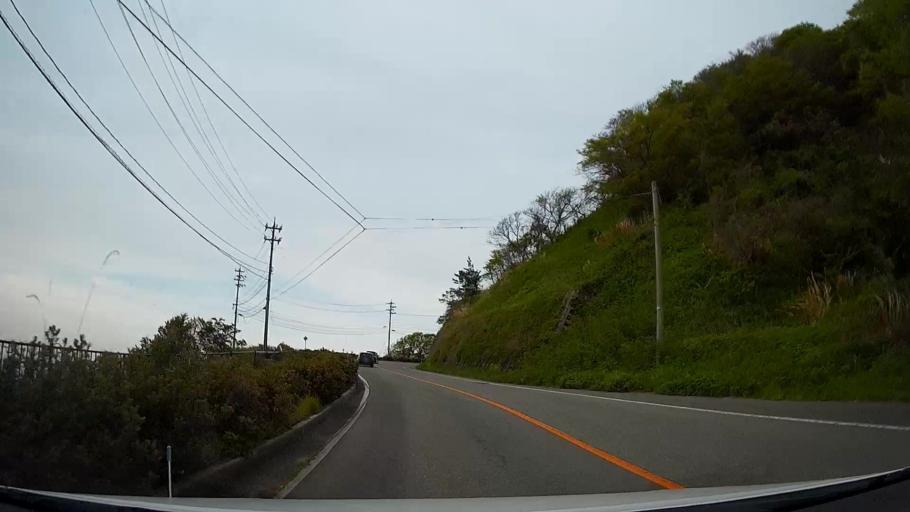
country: JP
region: Ishikawa
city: Nanao
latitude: 37.4007
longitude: 136.9430
